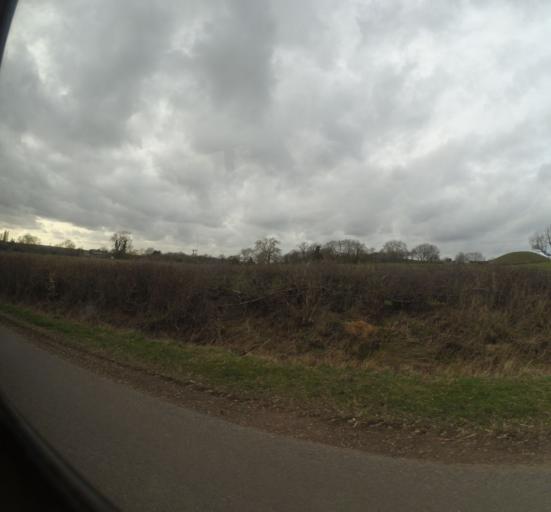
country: GB
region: England
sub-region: Warwickshire
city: Brandon
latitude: 52.4106
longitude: -1.3546
